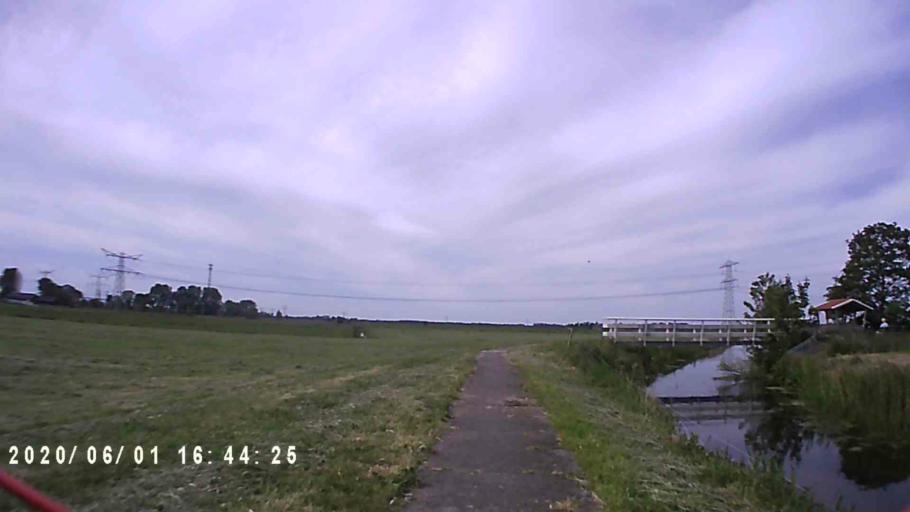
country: NL
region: Friesland
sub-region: Gemeente Tytsjerksteradiel
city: Tytsjerk
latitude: 53.1853
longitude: 5.8836
